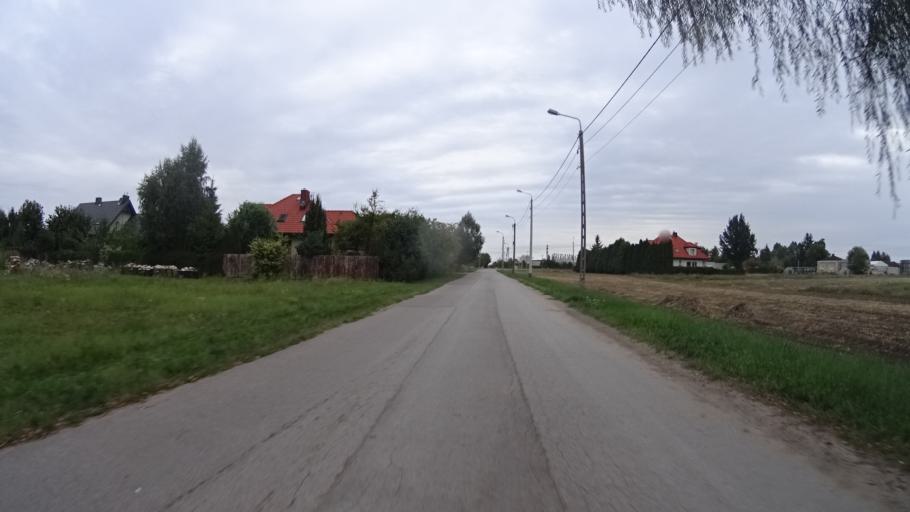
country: PL
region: Masovian Voivodeship
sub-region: Powiat warszawski zachodni
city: Ozarow Mazowiecki
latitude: 52.2451
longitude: 20.7859
